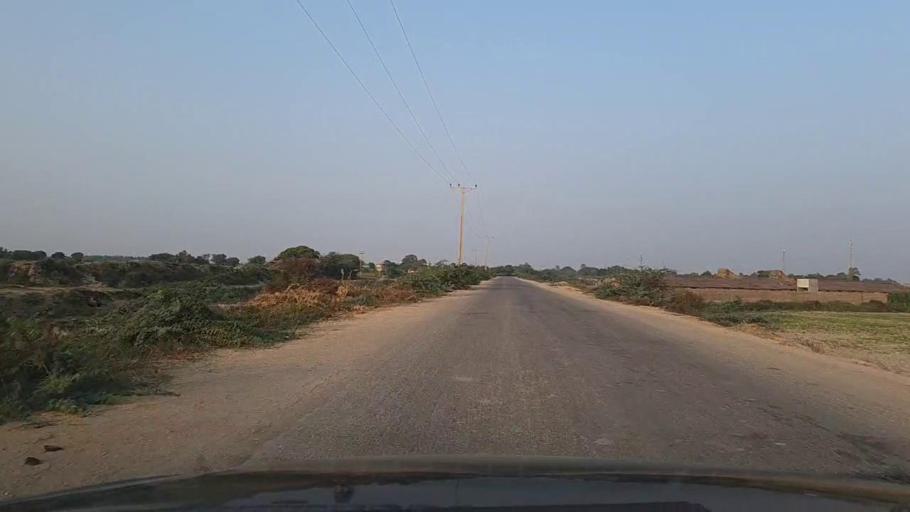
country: PK
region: Sindh
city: Mirpur Sakro
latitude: 24.5444
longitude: 67.8354
